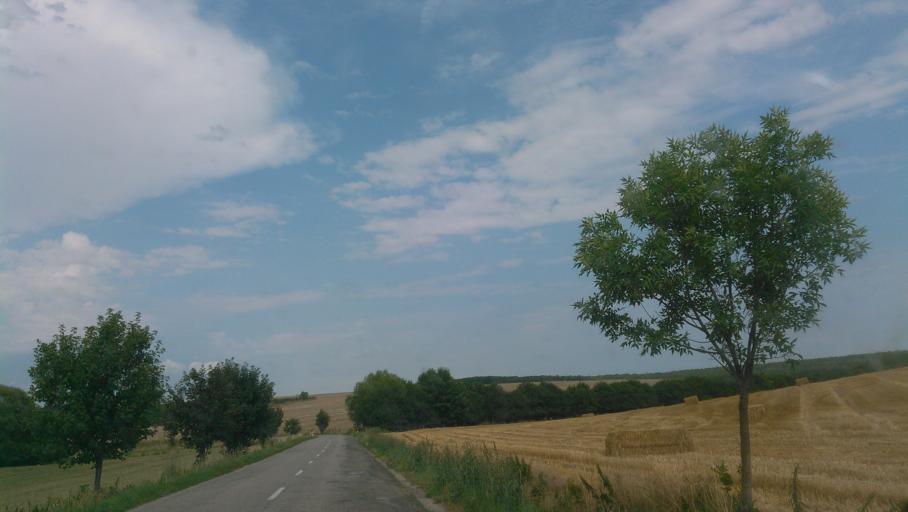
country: SK
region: Nitriansky
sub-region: Okres Nitra
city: Nitra
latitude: 48.5009
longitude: 18.0598
